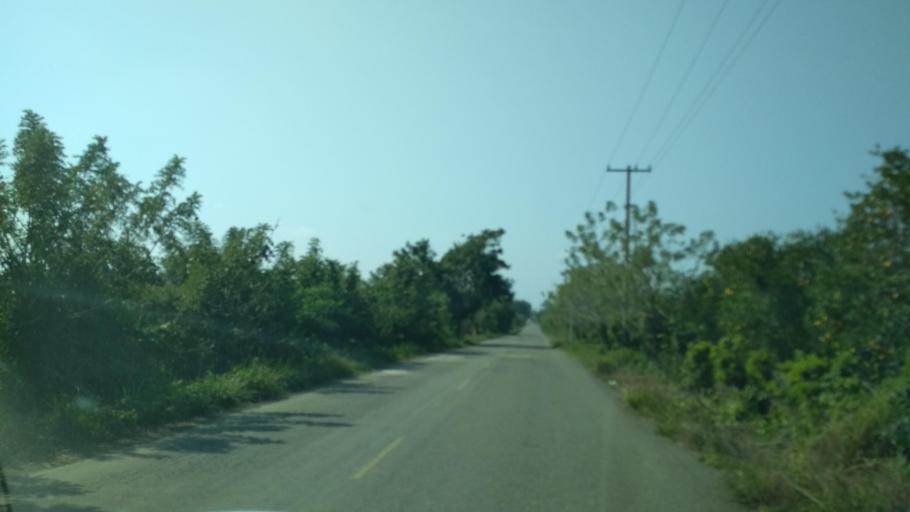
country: MX
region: Puebla
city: San Jose Acateno
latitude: 20.2003
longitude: -97.1820
